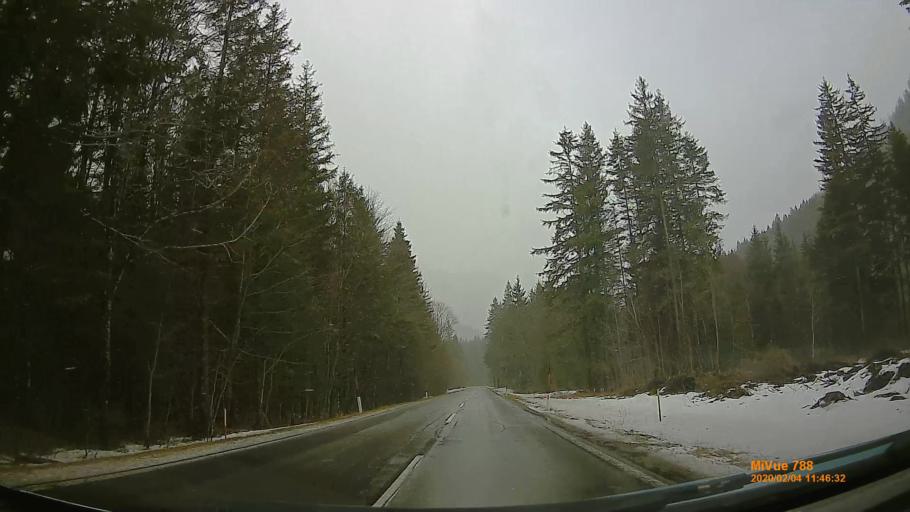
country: AT
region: Styria
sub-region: Politischer Bezirk Bruck-Muerzzuschlag
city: Muerzsteg
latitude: 47.7019
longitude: 15.4789
